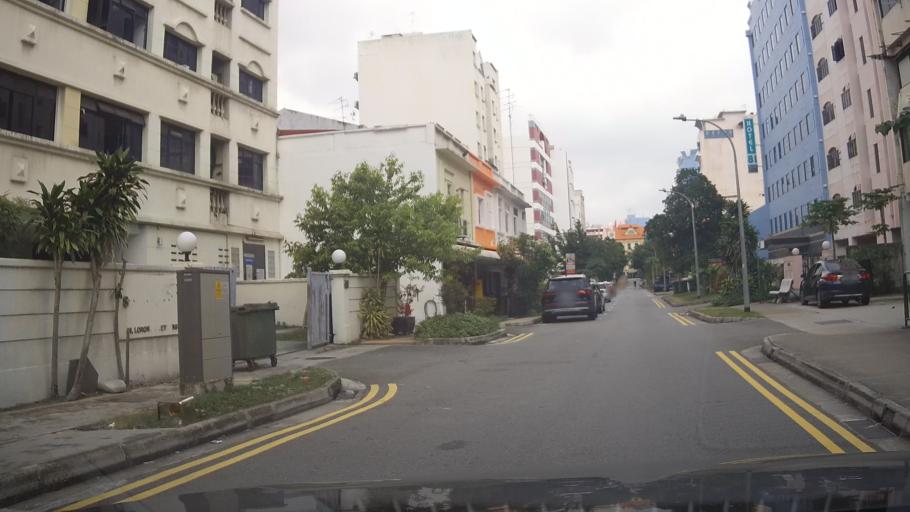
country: SG
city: Singapore
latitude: 1.3099
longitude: 103.8779
